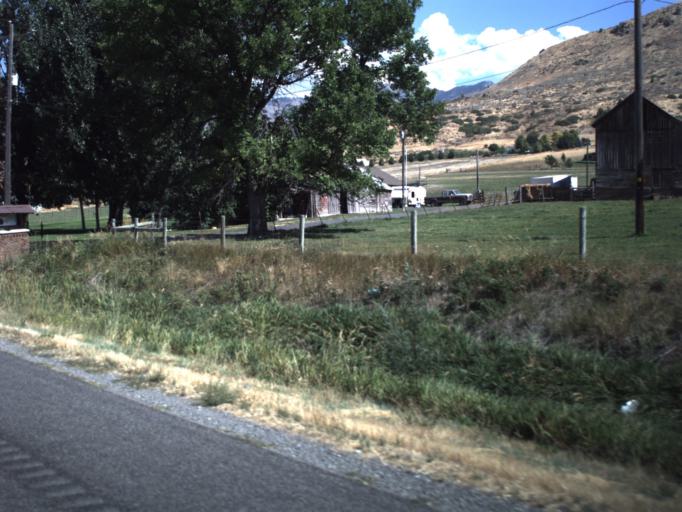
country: US
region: Utah
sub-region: Cache County
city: Smithfield
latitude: 41.8744
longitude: -111.8250
